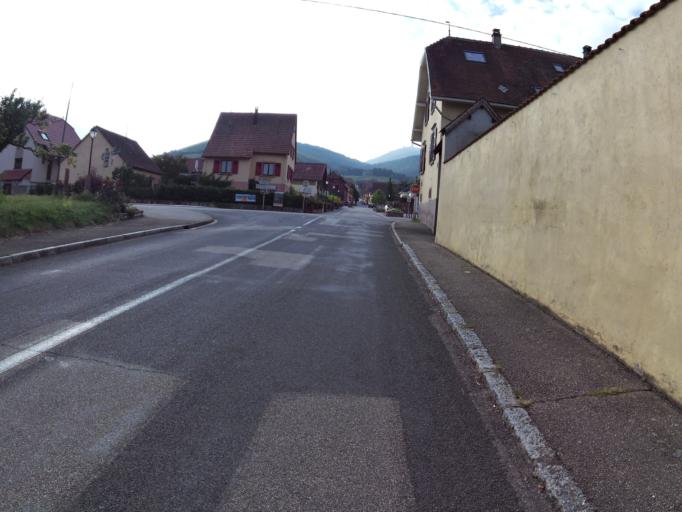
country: FR
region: Alsace
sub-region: Departement du Bas-Rhin
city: Kintzheim
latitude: 48.2409
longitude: 7.3851
